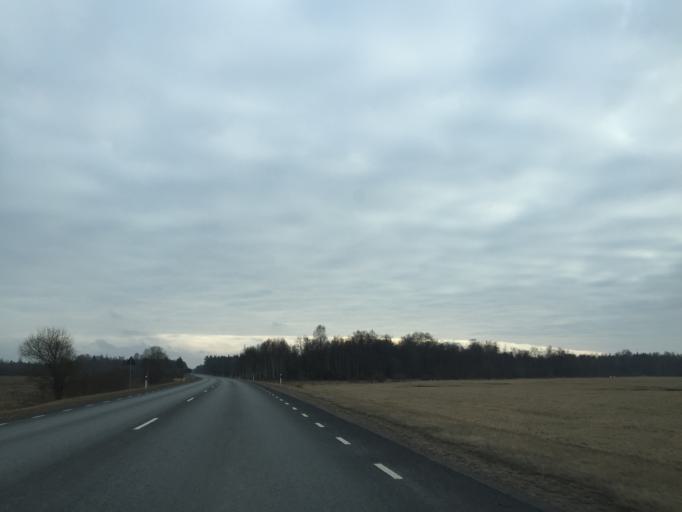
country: EE
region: Saare
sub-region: Orissaare vald
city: Orissaare
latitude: 58.5116
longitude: 22.8748
